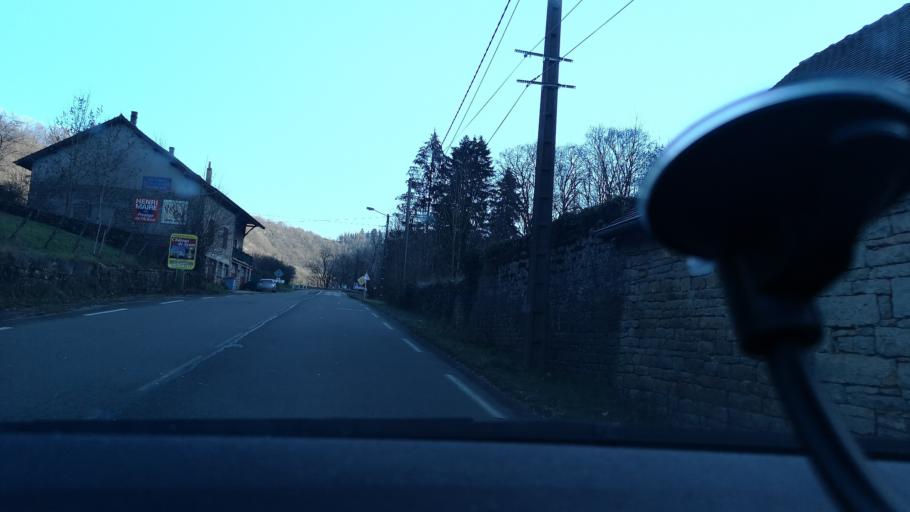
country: FR
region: Franche-Comte
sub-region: Departement du Jura
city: Poligny
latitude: 46.8243
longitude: 5.7257
